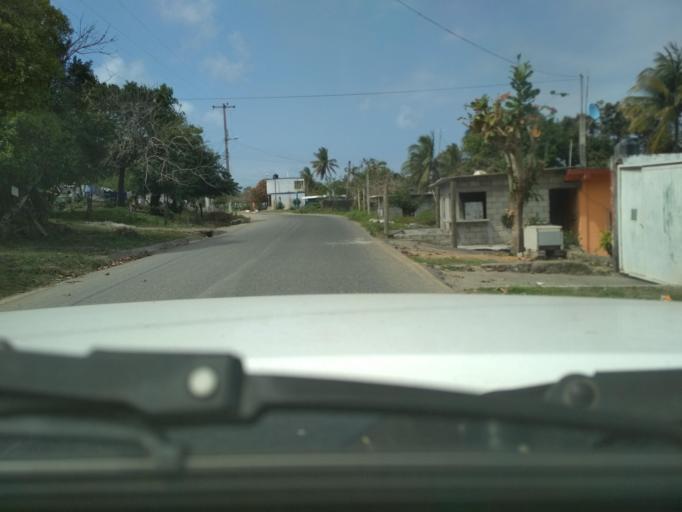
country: MX
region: Veracruz
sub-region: Veracruz
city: Delfino Victoria (Santa Fe)
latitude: 19.2533
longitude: -96.2634
